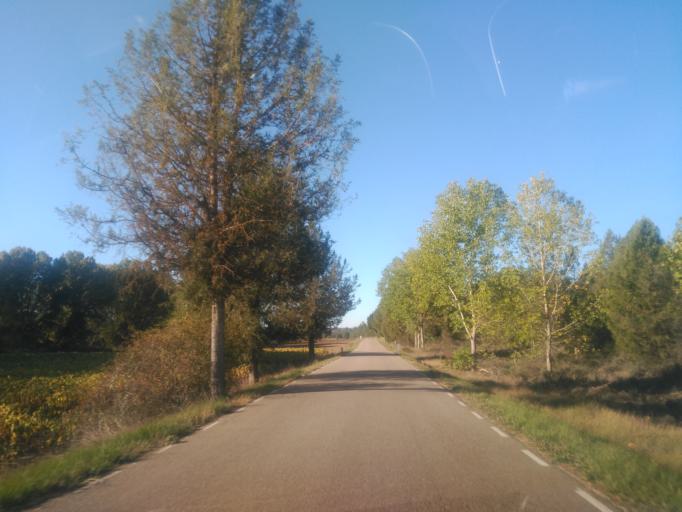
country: ES
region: Castille and Leon
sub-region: Provincia de Burgos
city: Brazacorta
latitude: 41.7073
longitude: -3.3893
